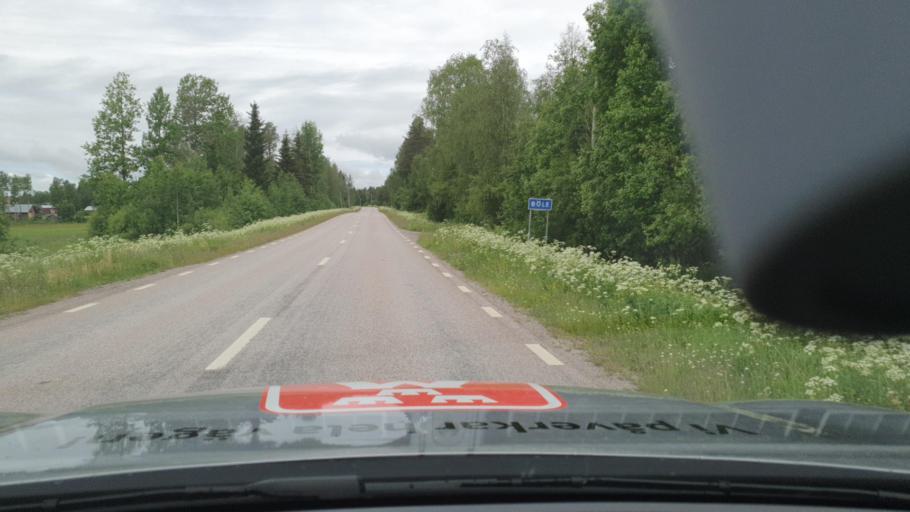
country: SE
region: Norrbotten
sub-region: Lulea Kommun
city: Ranea
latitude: 65.8851
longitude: 22.2648
